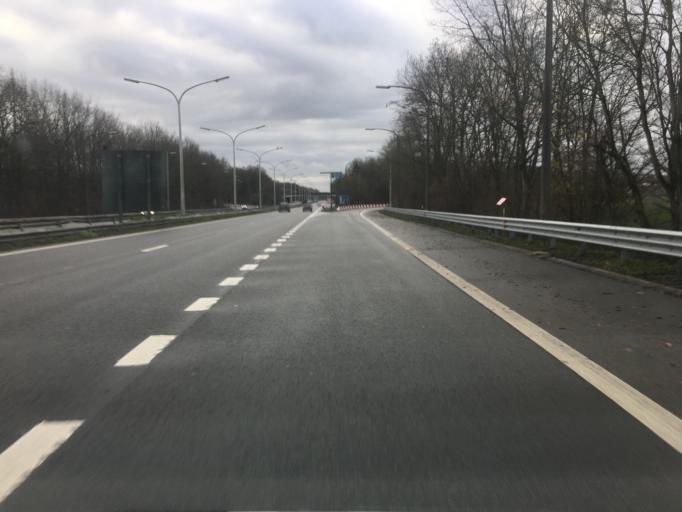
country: BE
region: Wallonia
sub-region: Province du Hainaut
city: Manage
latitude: 50.5037
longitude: 4.2119
